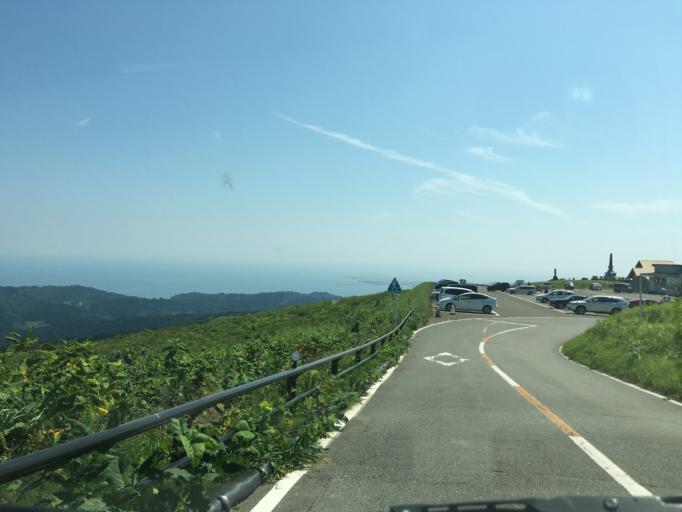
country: JP
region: Akita
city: Tenno
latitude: 39.9326
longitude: 139.8766
